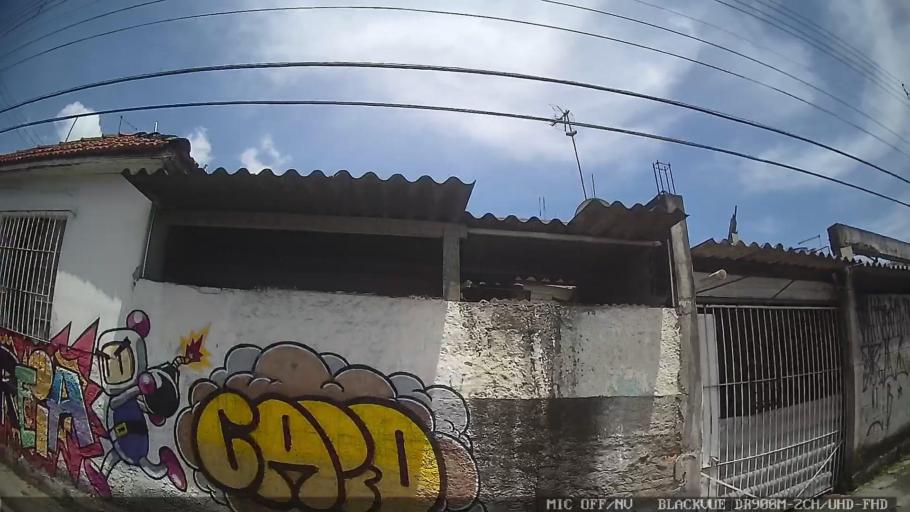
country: BR
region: Sao Paulo
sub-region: Suzano
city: Suzano
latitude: -23.5327
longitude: -46.3110
